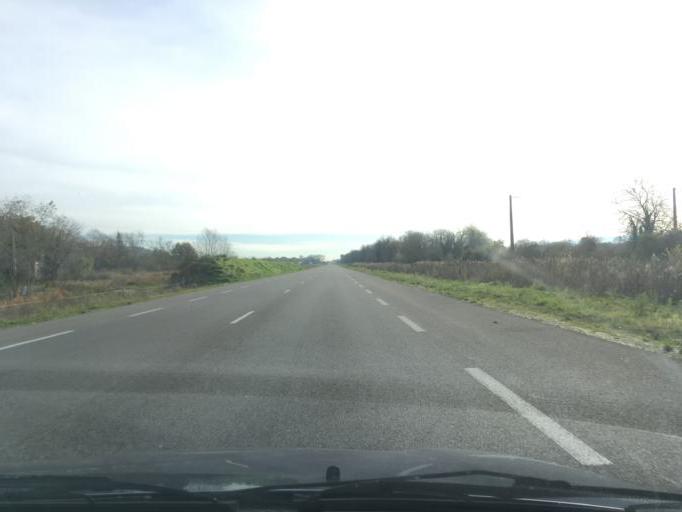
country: FR
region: Provence-Alpes-Cote d'Azur
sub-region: Departement du Vaucluse
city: Cadenet
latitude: 43.7187
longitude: 5.3962
